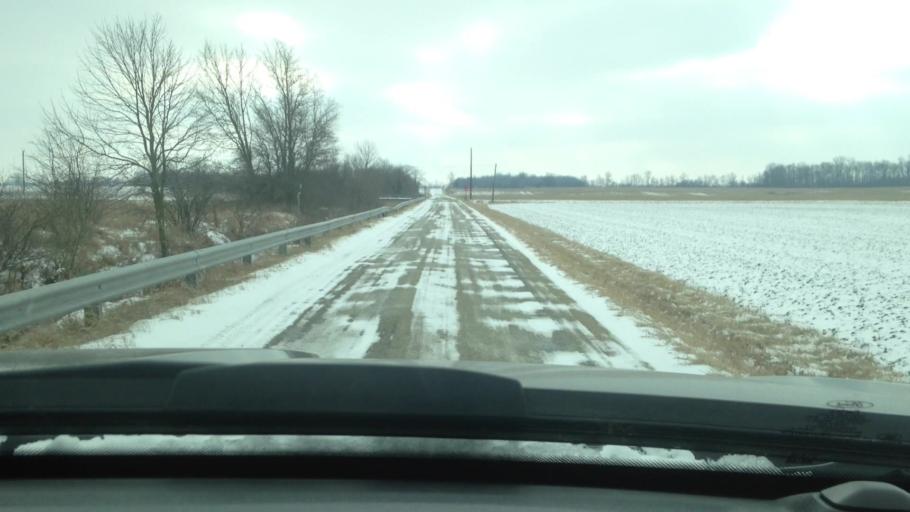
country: US
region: Indiana
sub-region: Randolph County
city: Union City
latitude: 40.2672
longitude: -84.8623
